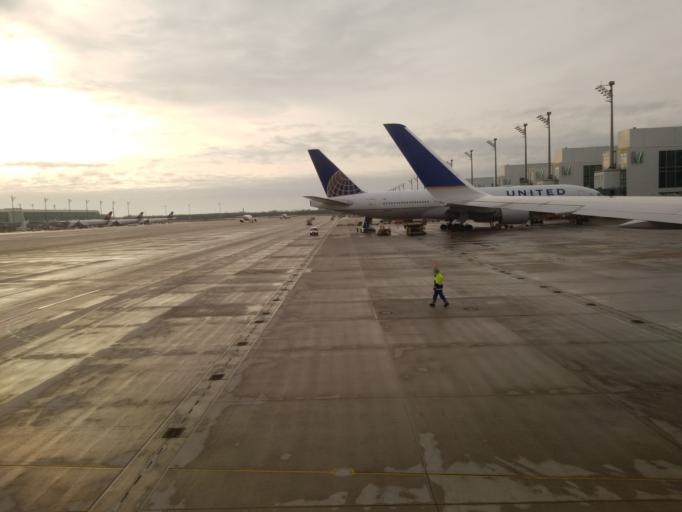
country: DE
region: Bavaria
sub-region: Upper Bavaria
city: Marzling
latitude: 48.3590
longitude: 11.7927
